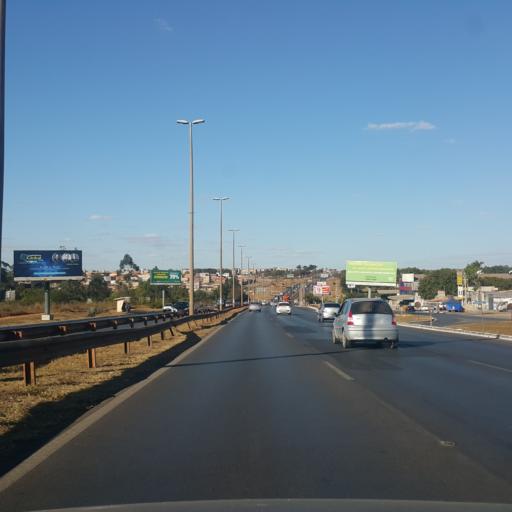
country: BR
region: Federal District
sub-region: Brasilia
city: Brasilia
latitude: -15.7869
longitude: -48.0082
